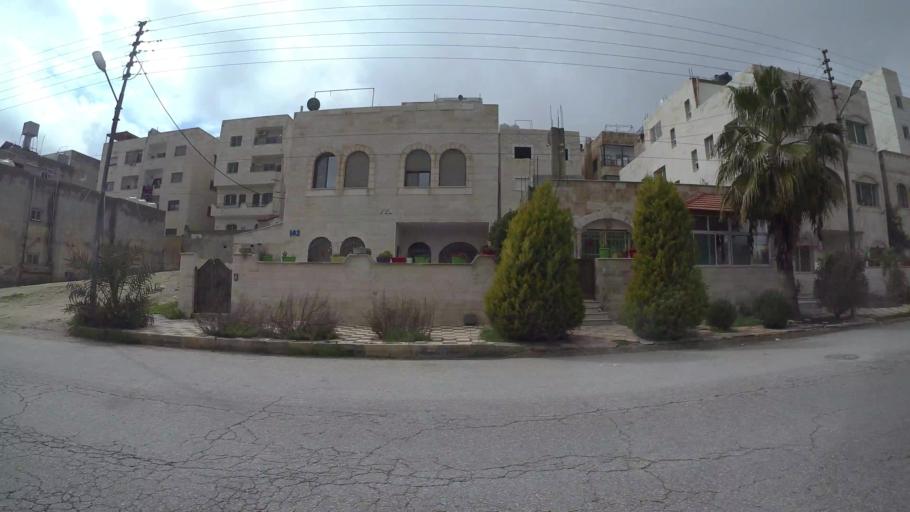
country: JO
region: Amman
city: Al Jubayhah
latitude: 32.0664
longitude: 35.8855
